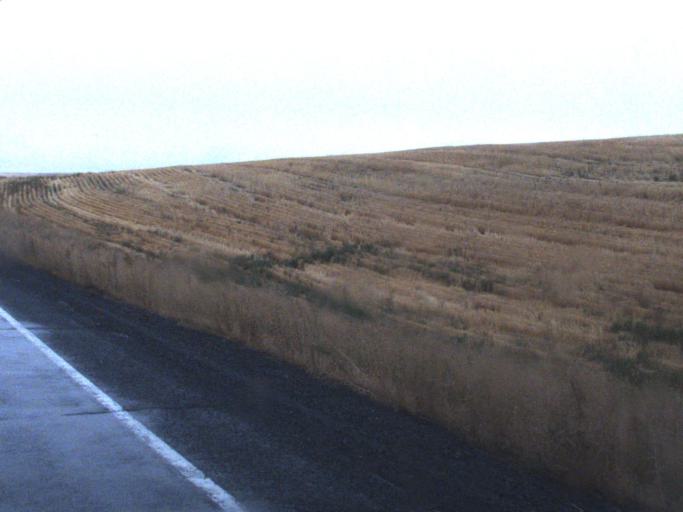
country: US
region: Washington
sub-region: Lincoln County
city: Davenport
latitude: 47.4782
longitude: -118.2037
